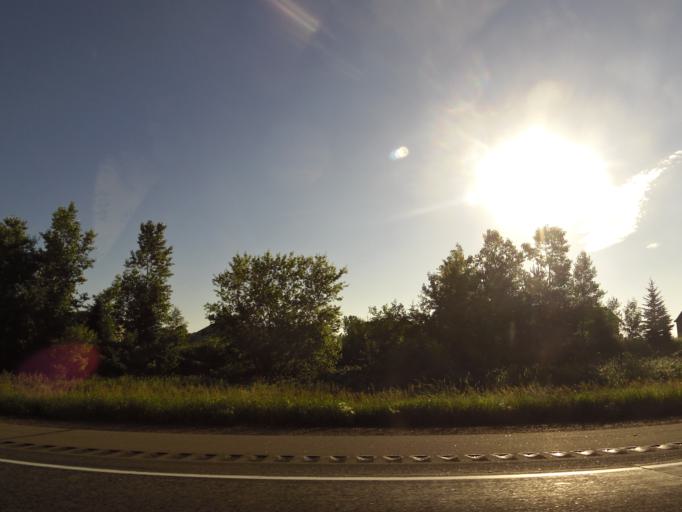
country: US
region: Minnesota
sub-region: Wright County
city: Monticello
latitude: 45.2863
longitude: -93.7537
